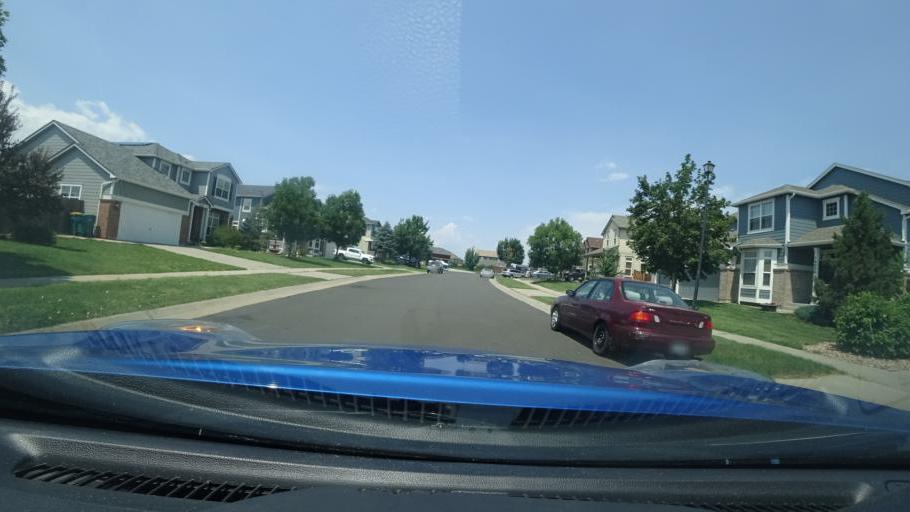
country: US
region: Colorado
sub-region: Adams County
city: Aurora
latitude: 39.6760
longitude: -104.7638
